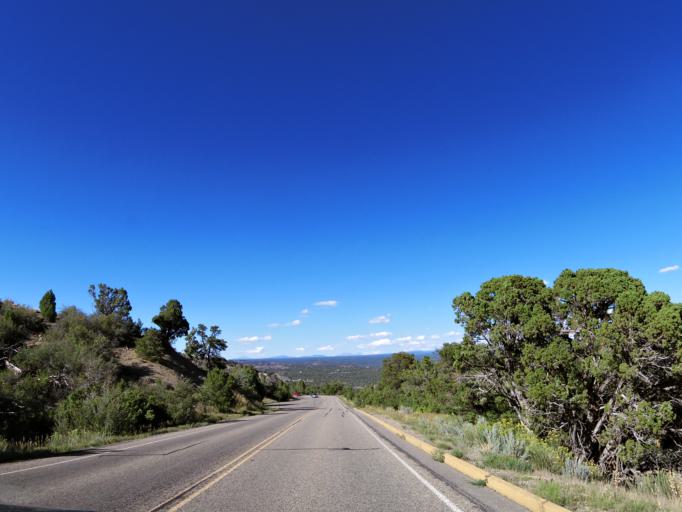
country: US
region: Colorado
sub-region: Montezuma County
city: Mancos
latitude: 37.3235
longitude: -108.4178
